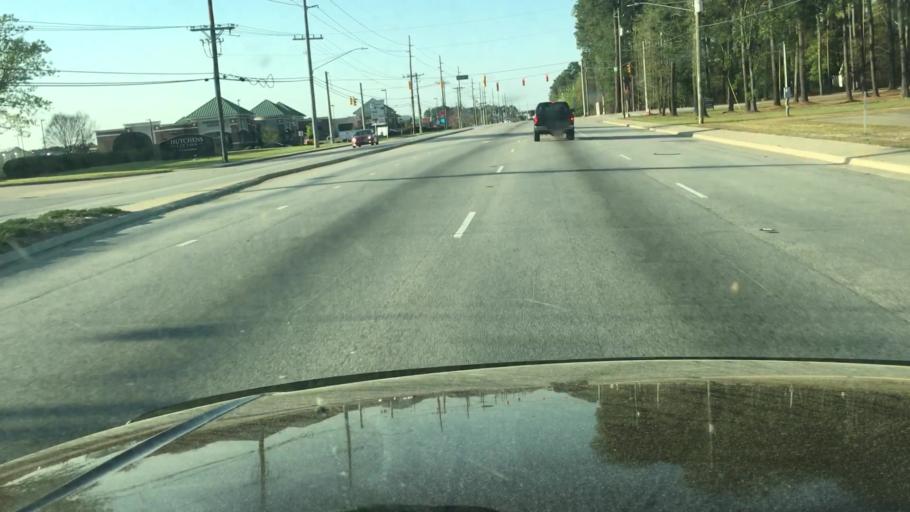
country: US
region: North Carolina
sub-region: Cumberland County
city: Fayetteville
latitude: 35.1192
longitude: -78.8797
